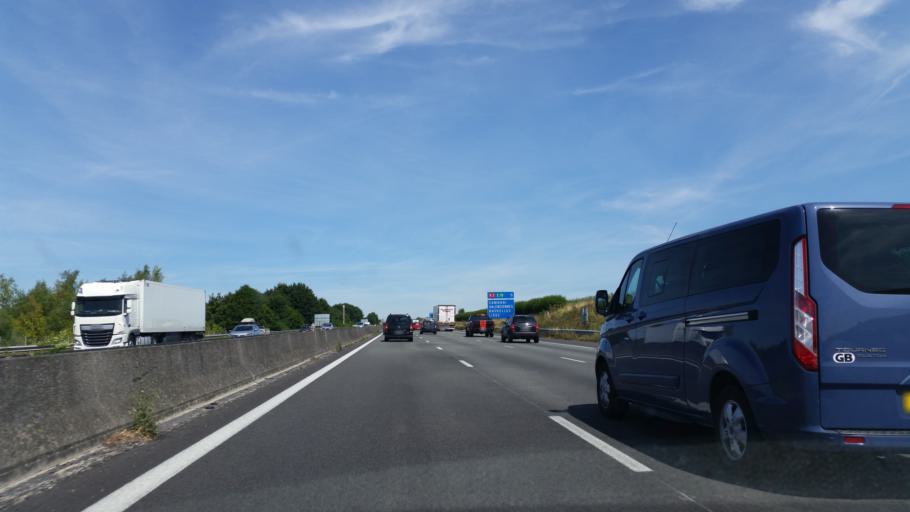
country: FR
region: Picardie
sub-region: Departement de la Somme
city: Peronne
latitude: 49.9771
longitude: 2.8658
